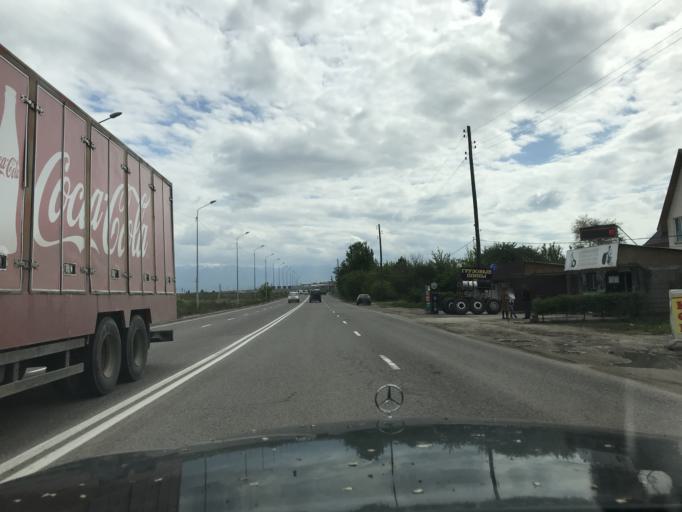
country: KZ
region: Almaty Oblysy
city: Burunday
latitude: 43.3527
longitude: 76.8347
